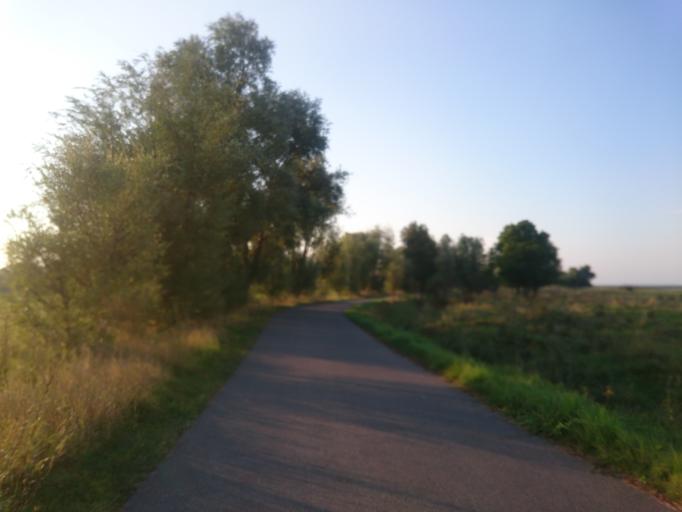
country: DE
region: Mecklenburg-Vorpommern
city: Barth
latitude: 54.3623
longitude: 12.8048
